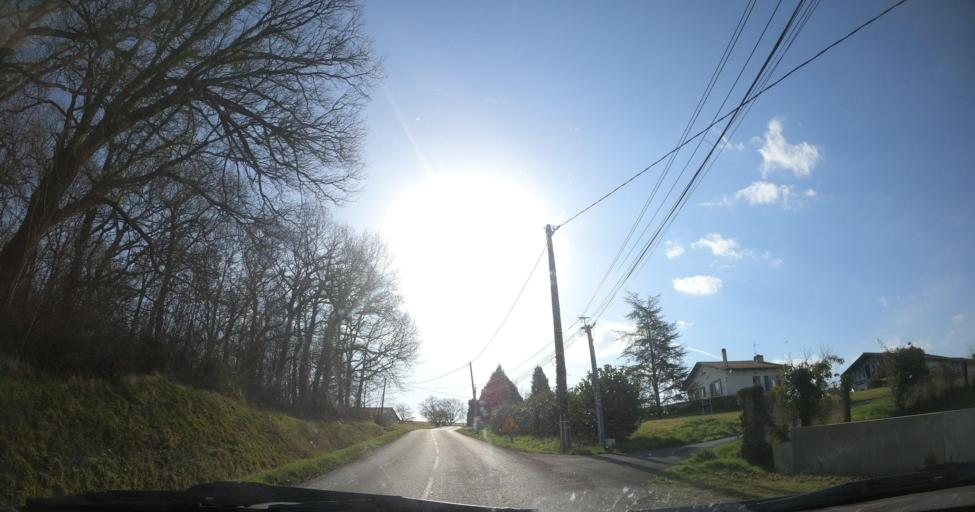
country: FR
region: Aquitaine
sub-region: Departement des Pyrenees-Atlantiques
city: Lahonce
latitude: 43.4513
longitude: -1.3705
